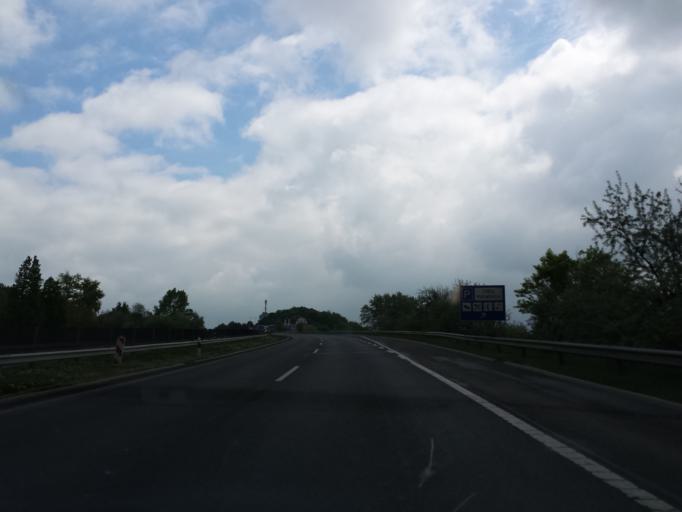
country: HU
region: Komarom-Esztergom
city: Tatabanya
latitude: 47.5809
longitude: 18.4099
